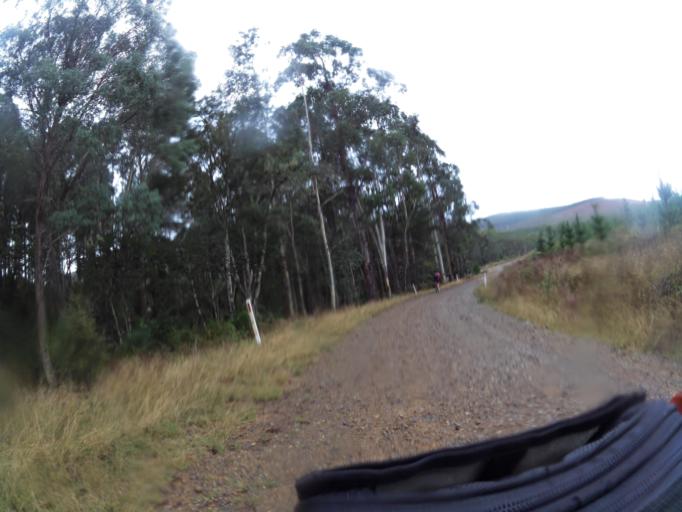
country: AU
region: New South Wales
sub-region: Greater Hume Shire
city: Holbrook
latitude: -36.2104
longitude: 147.5720
